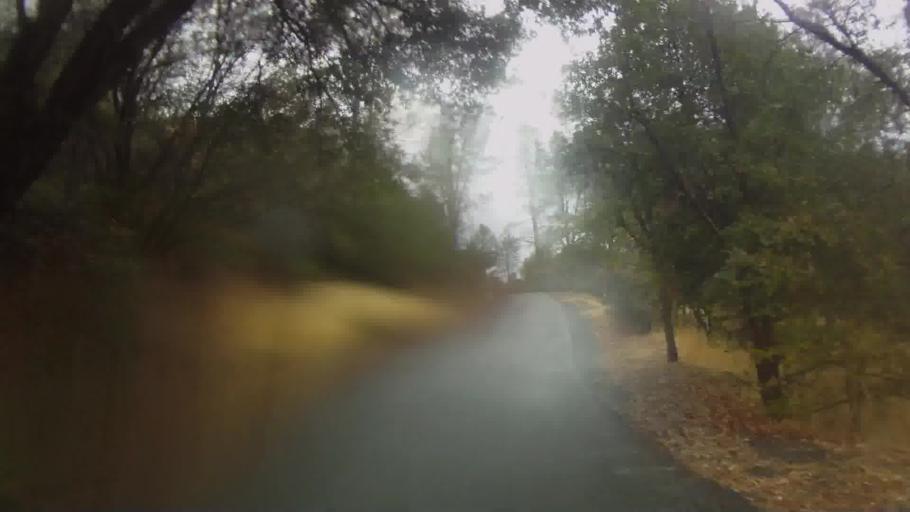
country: US
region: California
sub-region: Shasta County
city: Shasta
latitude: 40.5971
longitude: -122.4906
